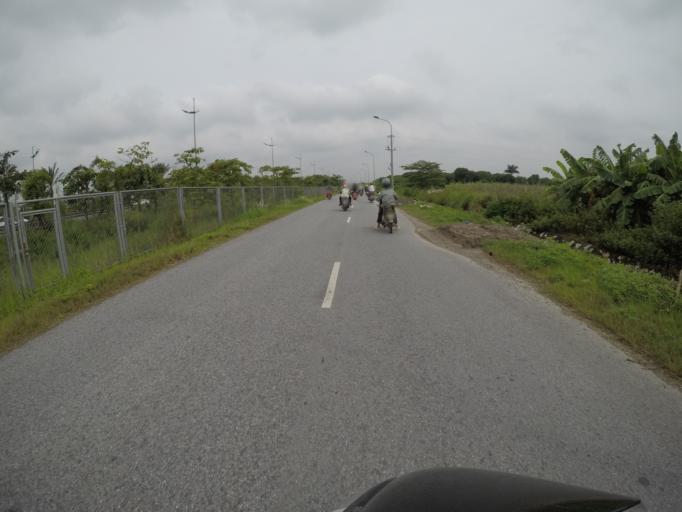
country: VN
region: Ha Noi
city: Dong Anh
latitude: 21.1578
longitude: 105.8198
